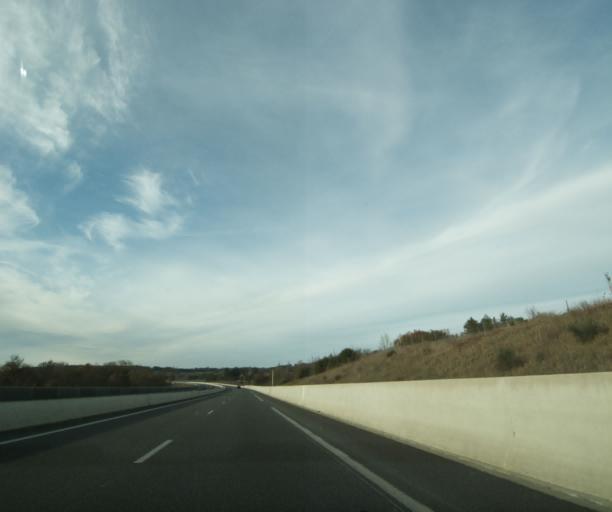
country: FR
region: Midi-Pyrenees
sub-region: Departement du Gers
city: Preignan
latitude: 43.6564
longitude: 0.6634
